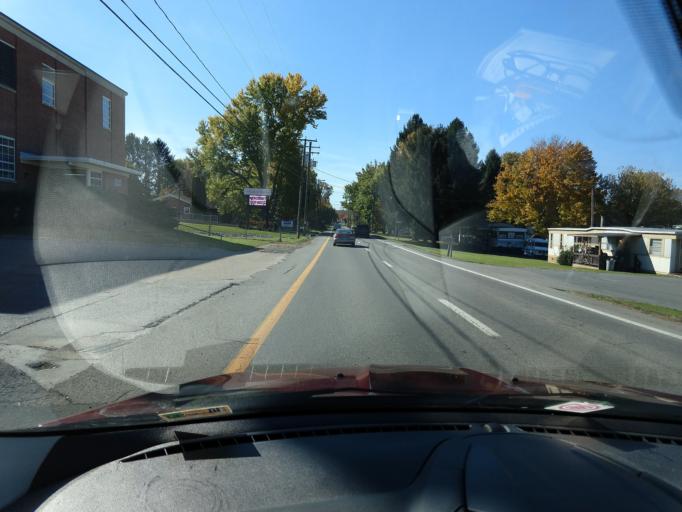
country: US
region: West Virginia
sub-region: Greenbrier County
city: Fairlea
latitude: 37.7828
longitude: -80.4574
